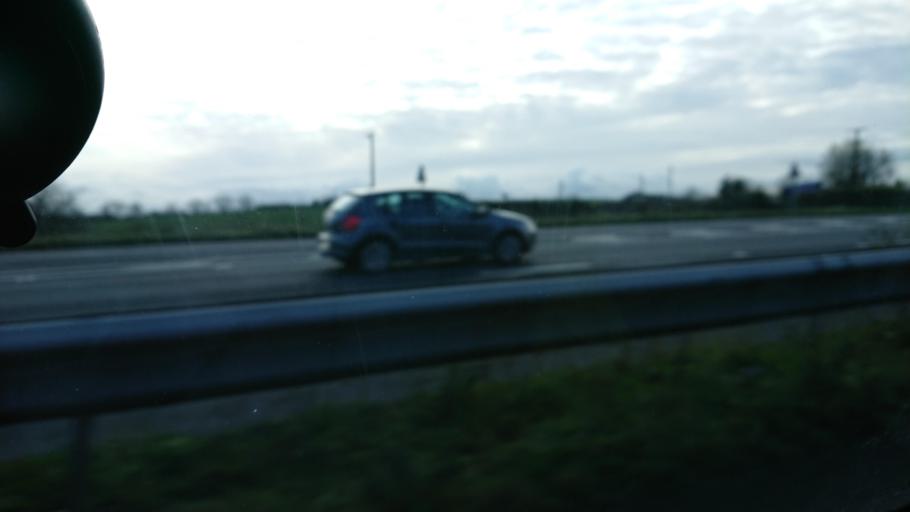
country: GB
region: England
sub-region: Devon
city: Yealmpton
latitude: 50.3828
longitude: -3.9804
